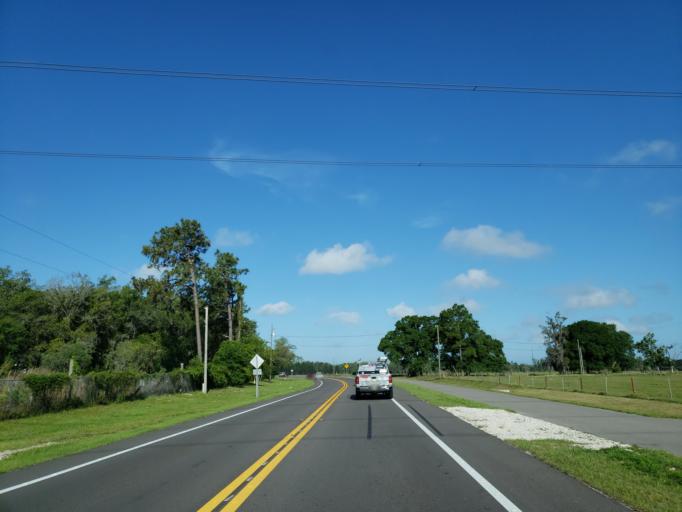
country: US
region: Florida
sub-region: Hillsborough County
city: Keystone
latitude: 28.1454
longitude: -82.6533
